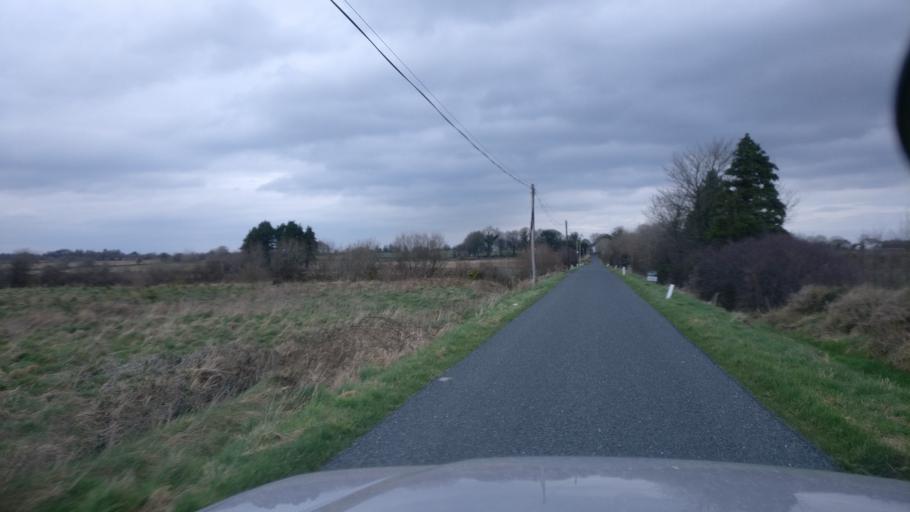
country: IE
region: Connaught
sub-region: County Galway
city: Loughrea
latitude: 53.2454
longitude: -8.5162
